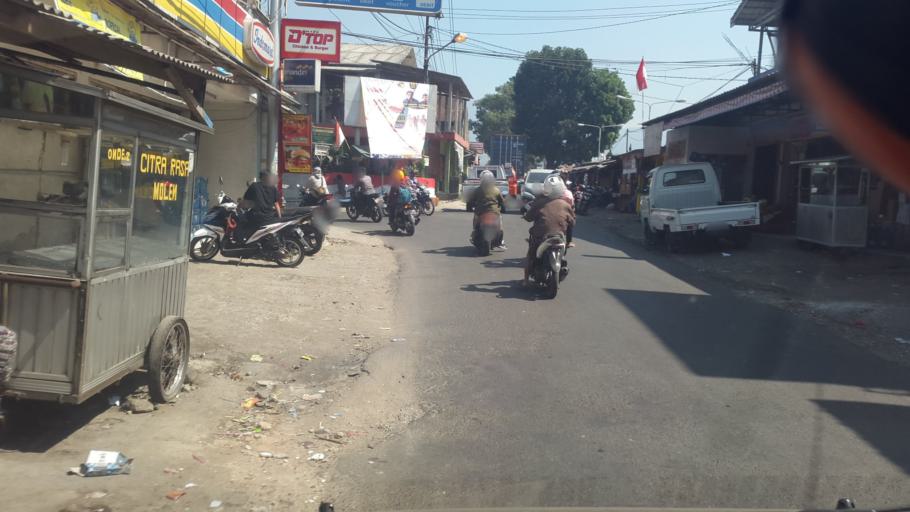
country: ID
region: West Java
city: Cicurug
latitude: -6.8275
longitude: 106.7361
